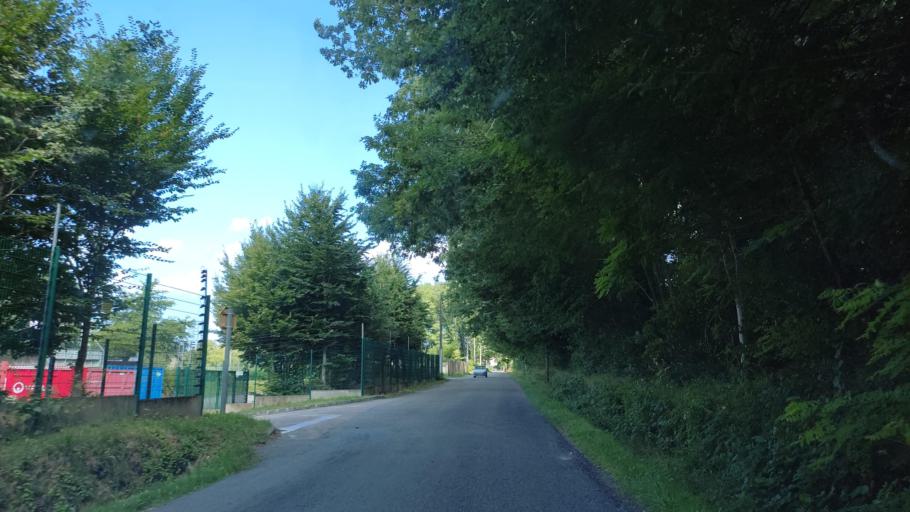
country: FR
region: Limousin
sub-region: Departement de la Haute-Vienne
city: Couzeix
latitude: 45.8549
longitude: 1.1892
